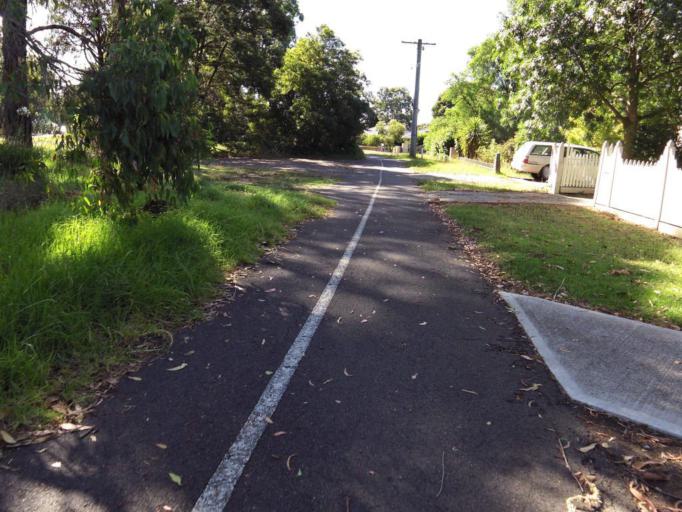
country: AU
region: Victoria
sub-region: Yarra Ranges
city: Kilsyth
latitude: -37.7951
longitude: 145.3235
